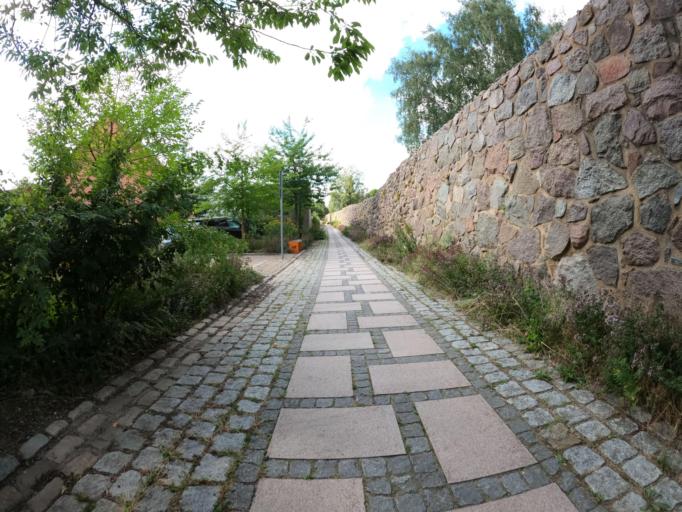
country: DE
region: Mecklenburg-Vorpommern
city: Woldegk
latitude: 53.4604
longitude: 13.5861
